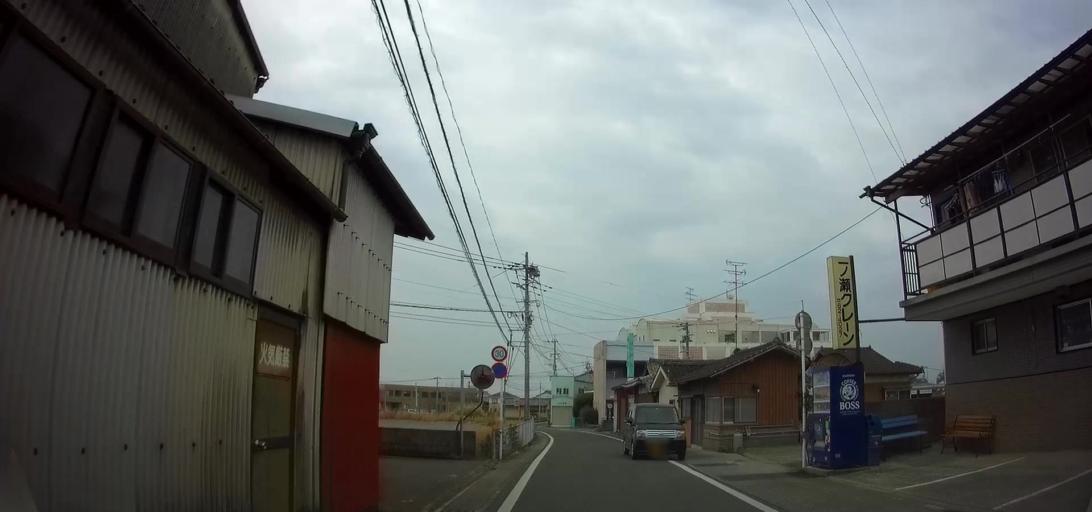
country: JP
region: Nagasaki
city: Shimabara
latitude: 32.6625
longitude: 130.3000
